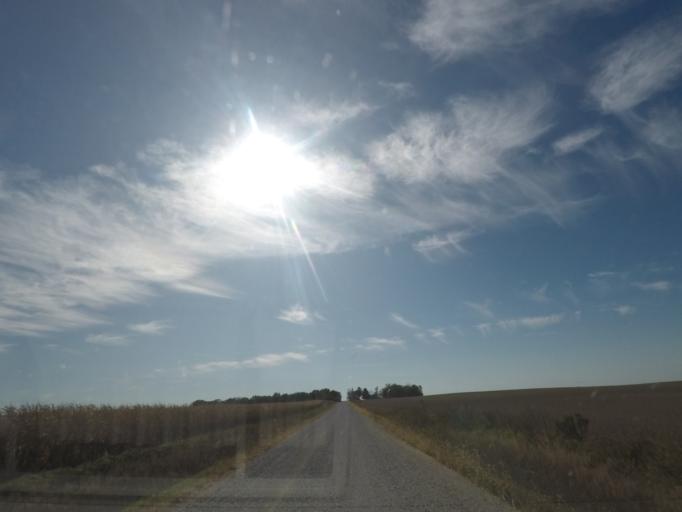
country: US
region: Iowa
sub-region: Story County
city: Nevada
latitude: 42.0543
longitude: -93.3291
